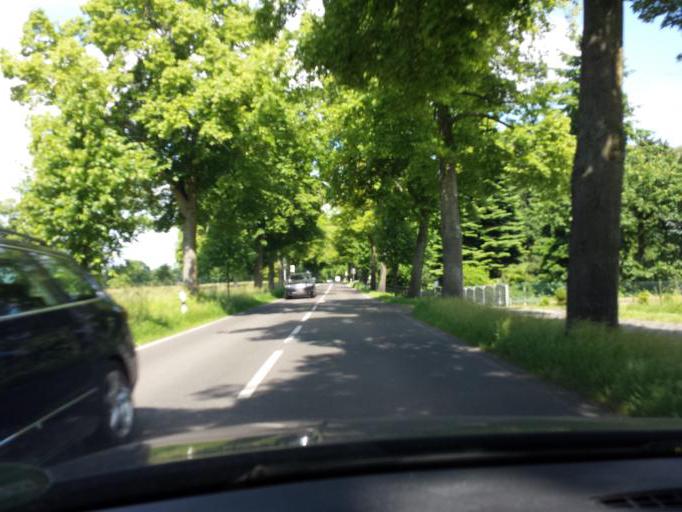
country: DE
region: Brandenburg
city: Kremmen
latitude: 52.8075
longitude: 13.0242
